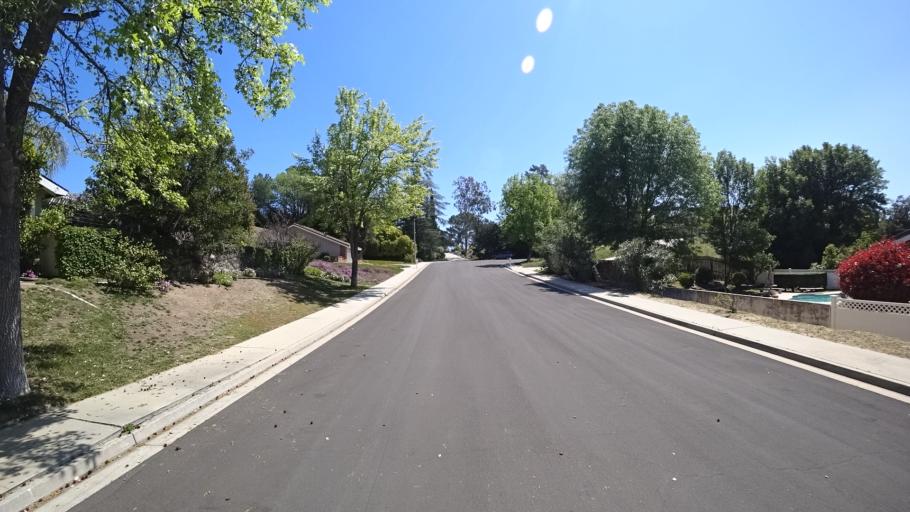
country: US
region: California
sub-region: Ventura County
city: Casa Conejo
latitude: 34.2007
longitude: -118.8918
